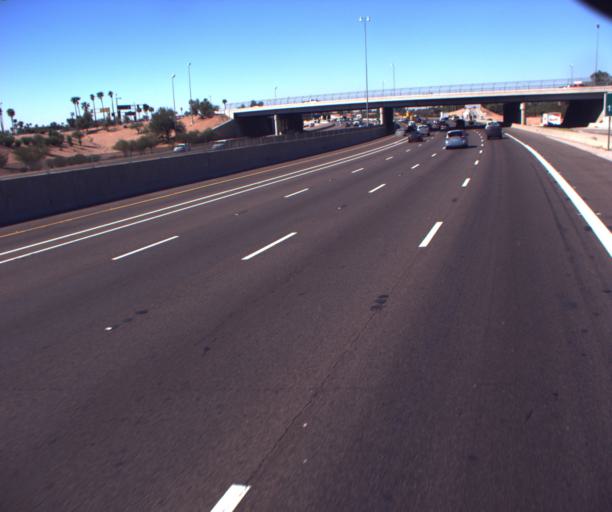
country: US
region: Arizona
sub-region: Maricopa County
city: Tempe Junction
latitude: 33.4081
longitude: -111.9709
